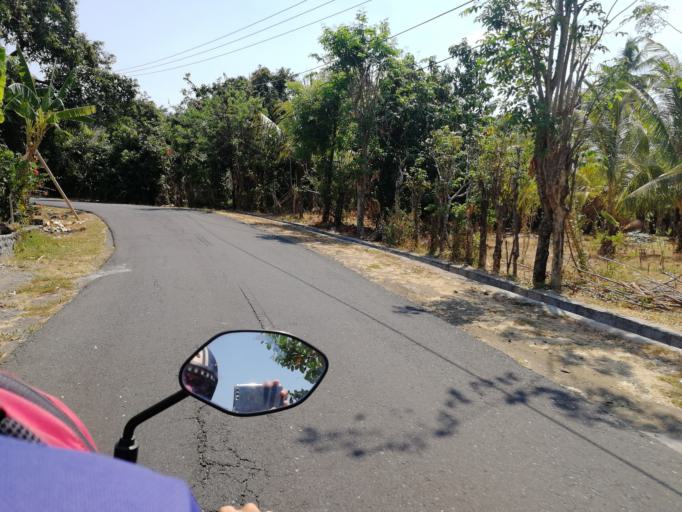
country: ID
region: Bali
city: Banjar Trunyan
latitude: -8.1225
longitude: 115.3288
